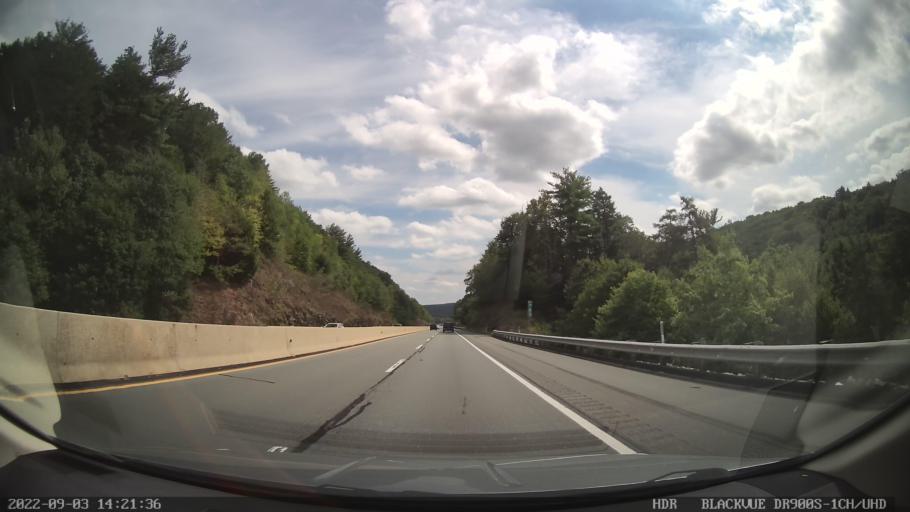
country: US
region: Pennsylvania
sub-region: Carbon County
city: Weissport East
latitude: 40.8697
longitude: -75.6542
